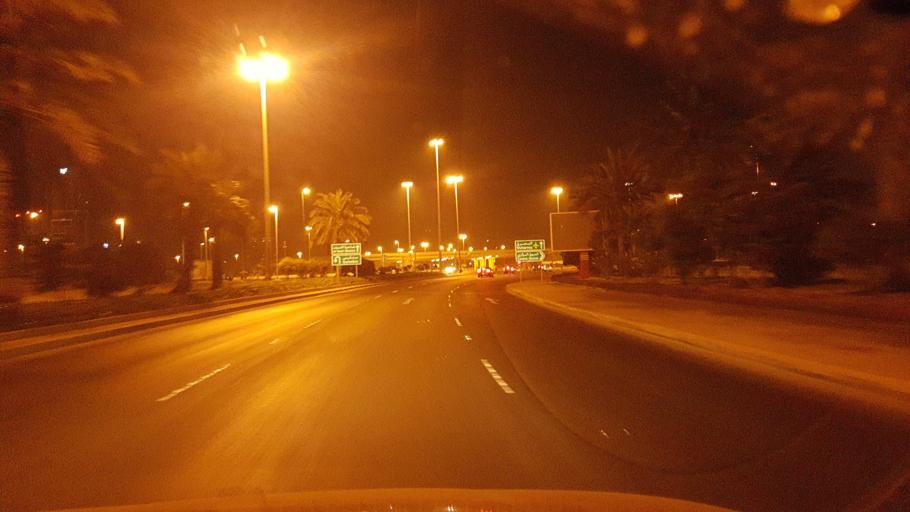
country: BH
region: Manama
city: Jidd Hafs
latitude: 26.2285
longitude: 50.5609
